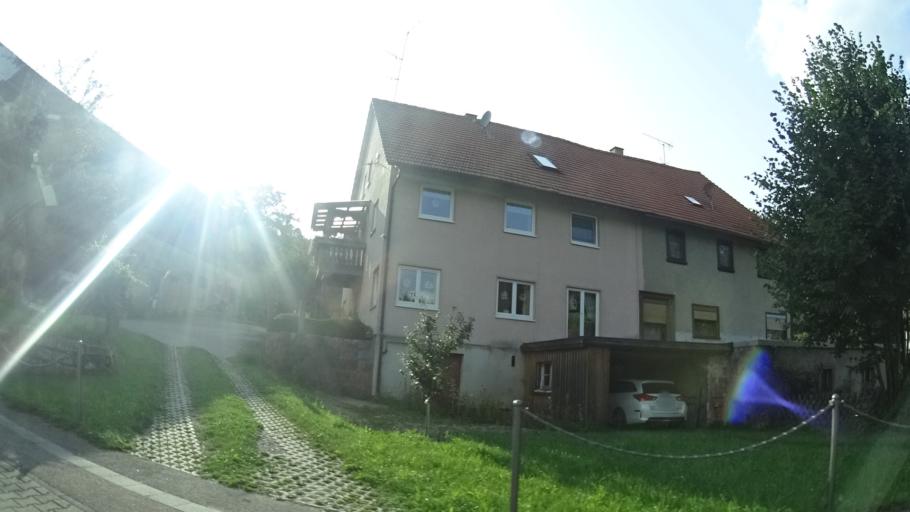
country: DE
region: Hesse
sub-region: Regierungsbezirk Darmstadt
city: Beerfelden
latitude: 49.5610
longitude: 9.0147
